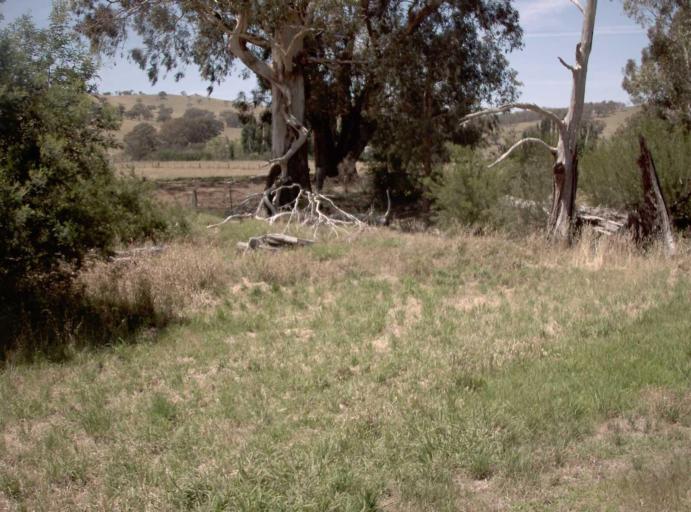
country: AU
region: Victoria
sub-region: East Gippsland
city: Bairnsdale
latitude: -37.2291
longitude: 147.7170
